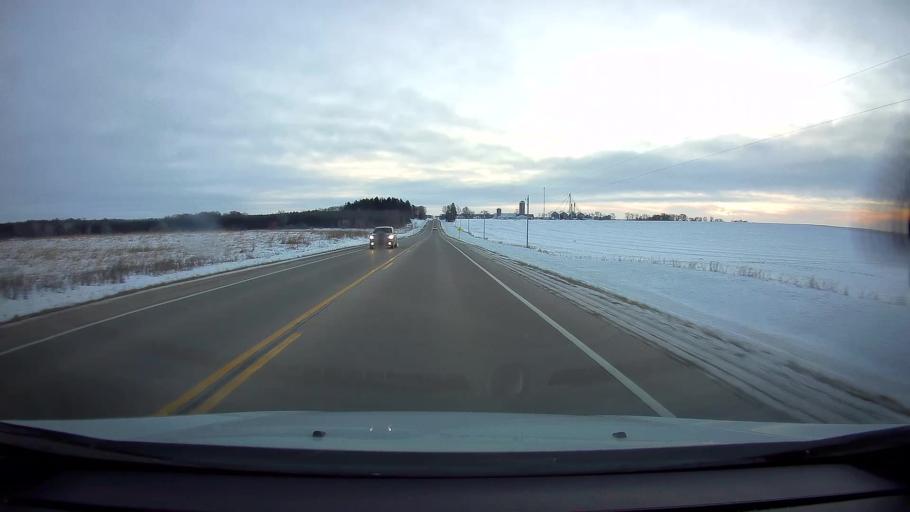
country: US
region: Wisconsin
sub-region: Saint Croix County
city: New Richmond
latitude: 45.1371
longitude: -92.4879
